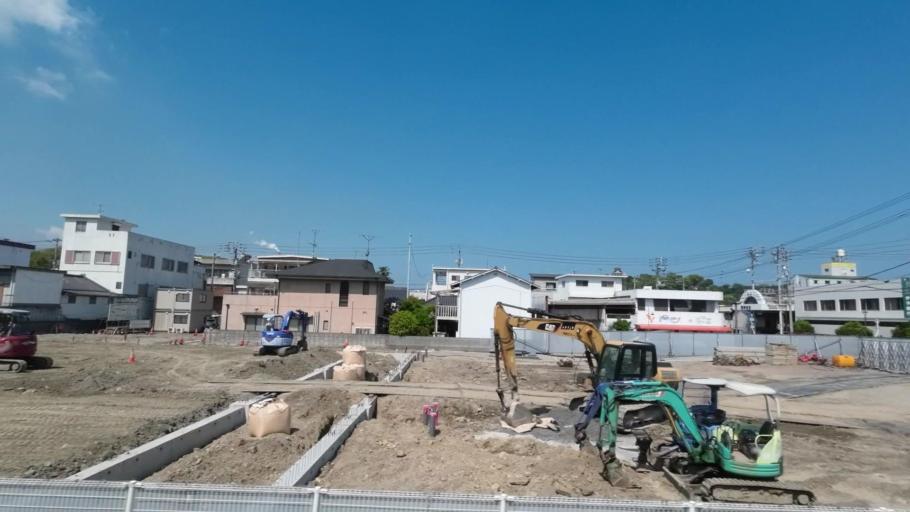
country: JP
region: Ehime
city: Kawanoecho
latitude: 34.0109
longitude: 133.5754
